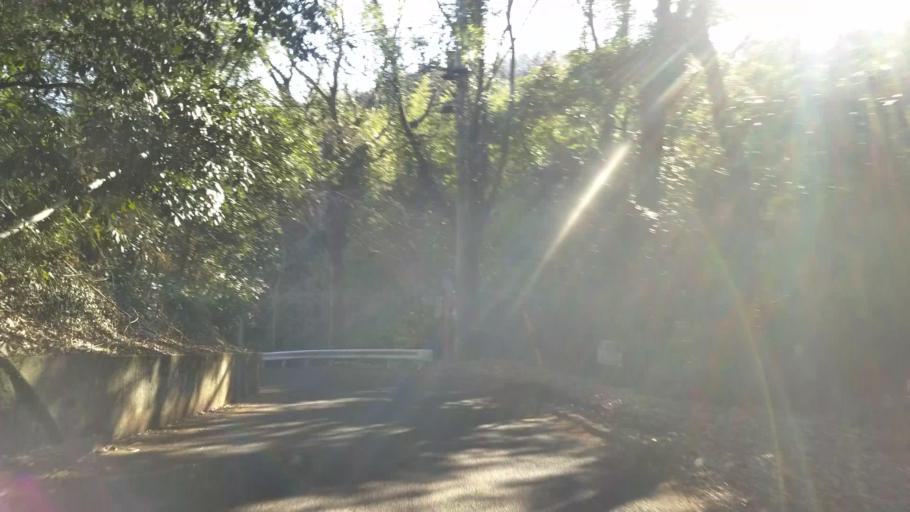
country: JP
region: Kanagawa
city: Hadano
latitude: 35.3715
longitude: 139.2494
